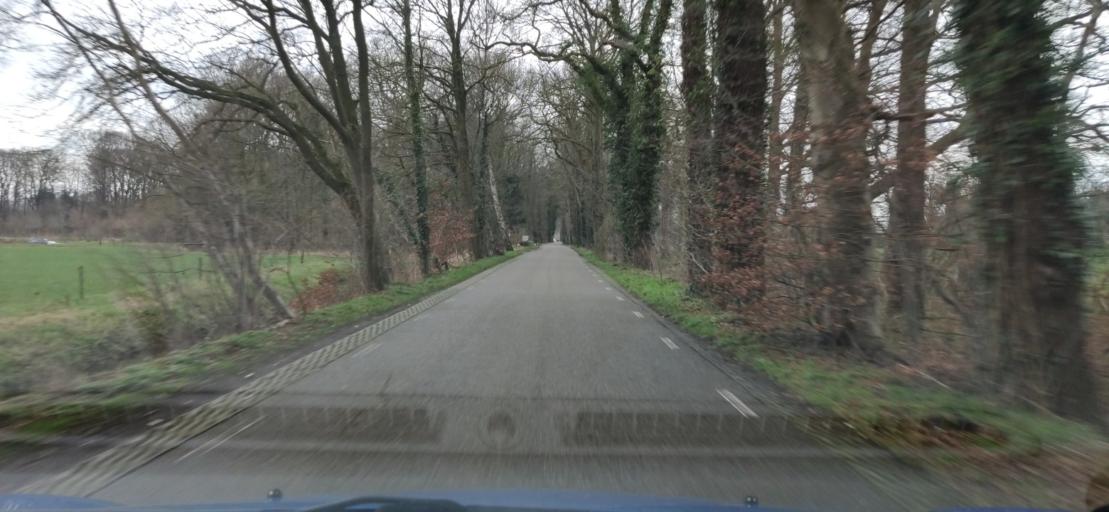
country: NL
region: Overijssel
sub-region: Gemeente Hengelo
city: Hengelo
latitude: 52.2209
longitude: 6.7722
